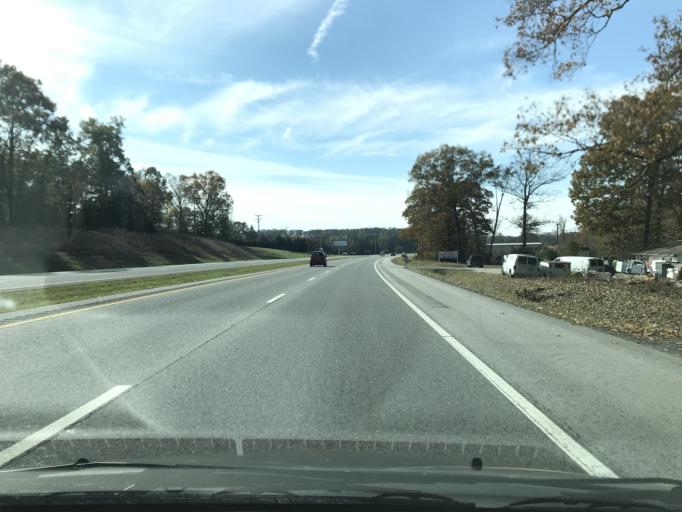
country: US
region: Tennessee
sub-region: Coffee County
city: Manchester
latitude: 35.4159
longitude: -86.1160
